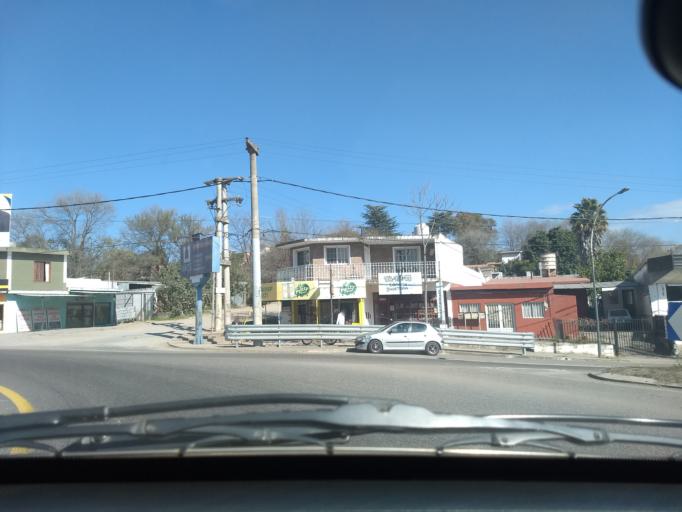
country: AR
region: Cordoba
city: Rio Ceballos
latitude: -31.1748
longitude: -64.3015
